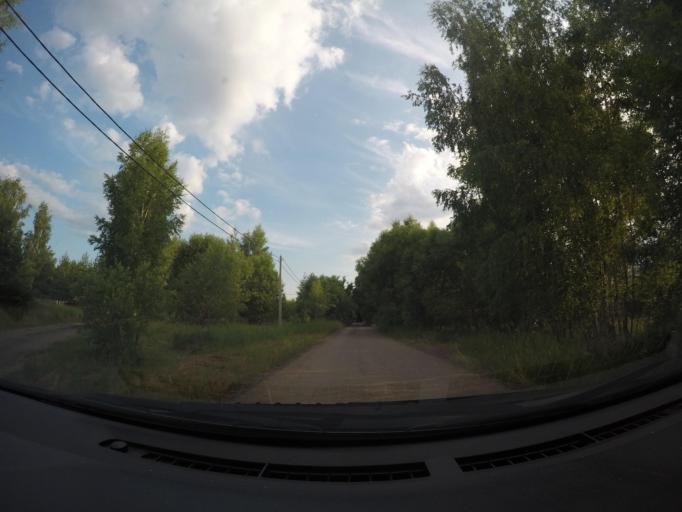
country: RU
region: Moskovskaya
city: Krasnyy Tkach
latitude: 55.4208
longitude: 39.2366
